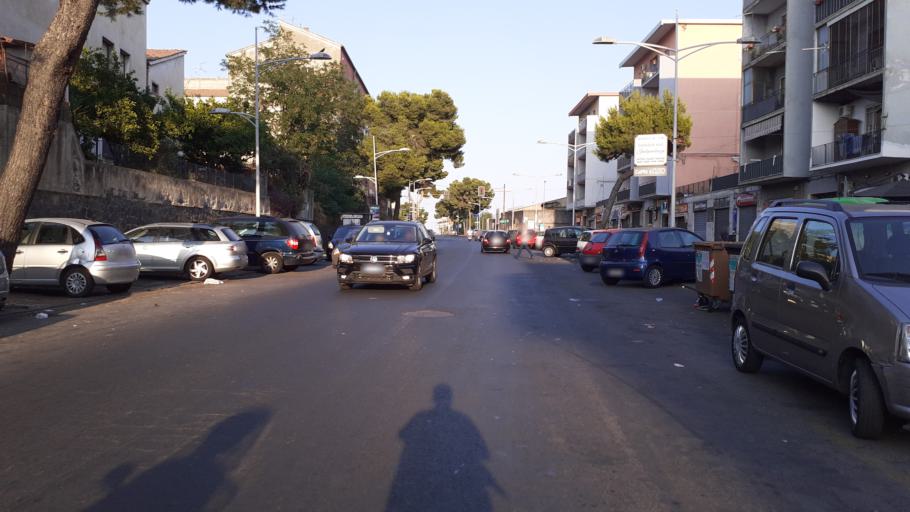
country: IT
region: Sicily
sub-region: Catania
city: Catania
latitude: 37.5018
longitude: 15.0616
